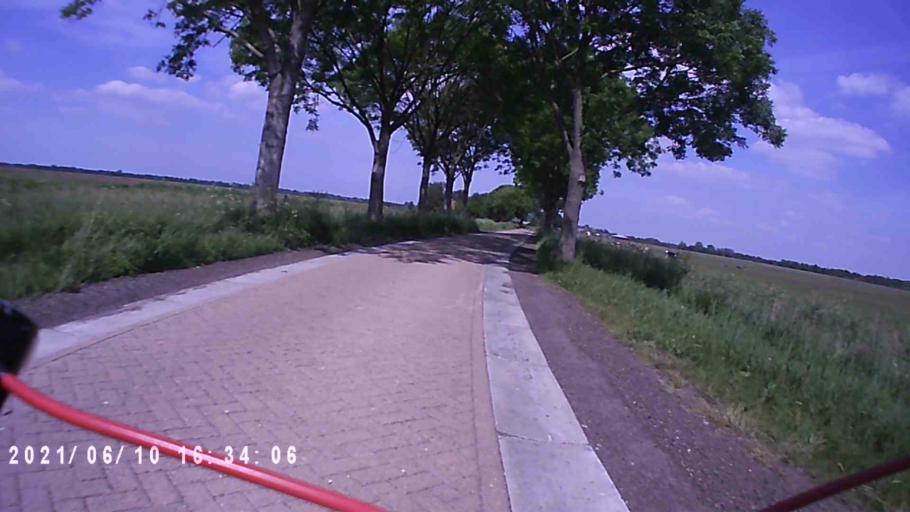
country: NL
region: Friesland
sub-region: Gemeente Achtkarspelen
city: Buitenpost
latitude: 53.2307
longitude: 6.1304
